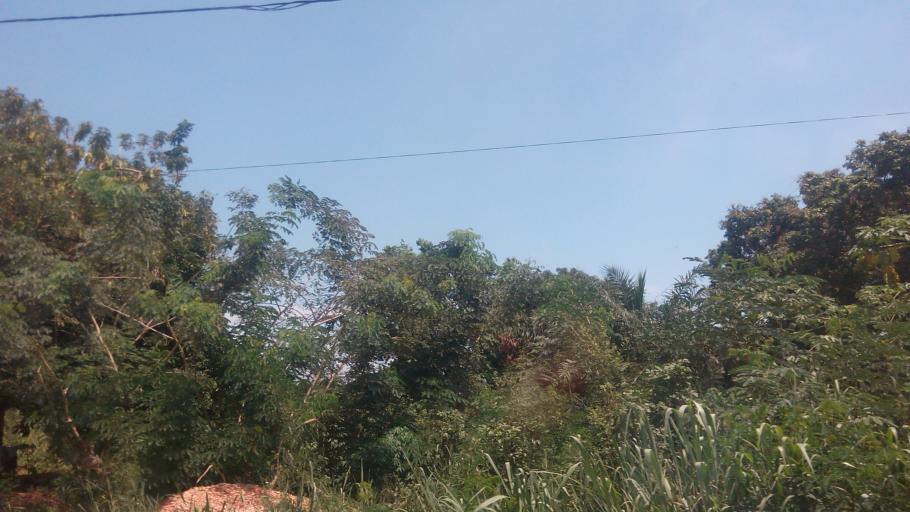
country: BJ
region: Mono
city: Come
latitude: 6.4004
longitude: 1.8905
